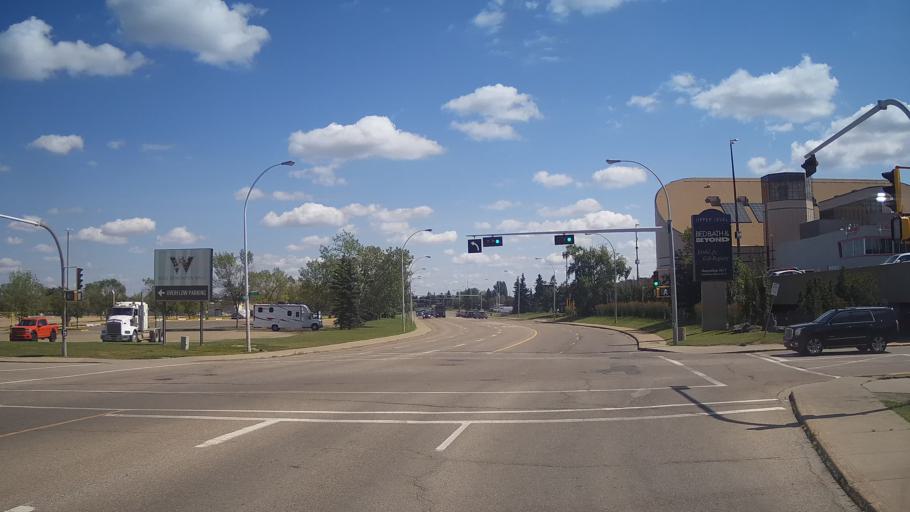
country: CA
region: Alberta
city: St. Albert
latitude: 53.5250
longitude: -113.6238
